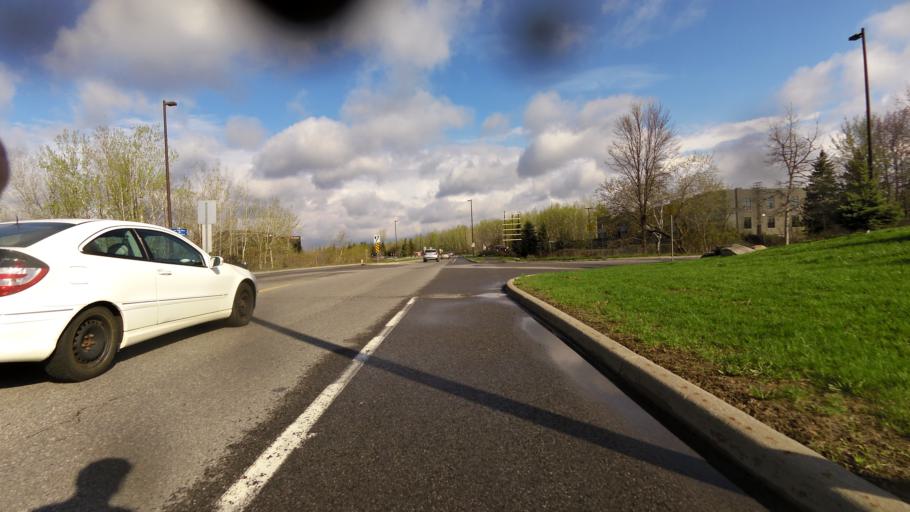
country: CA
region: Ontario
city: Bells Corners
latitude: 45.3475
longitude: -75.9028
